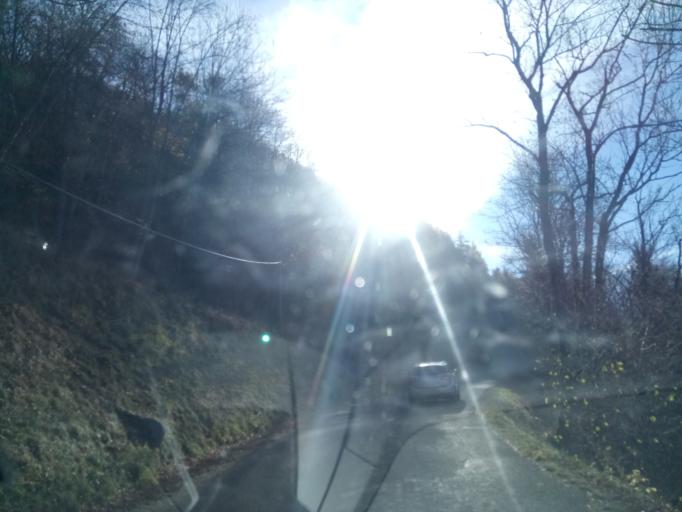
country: FR
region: Rhone-Alpes
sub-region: Departement de la Savoie
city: Saint-Michel-de-Maurienne
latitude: 45.2302
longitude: 6.4833
